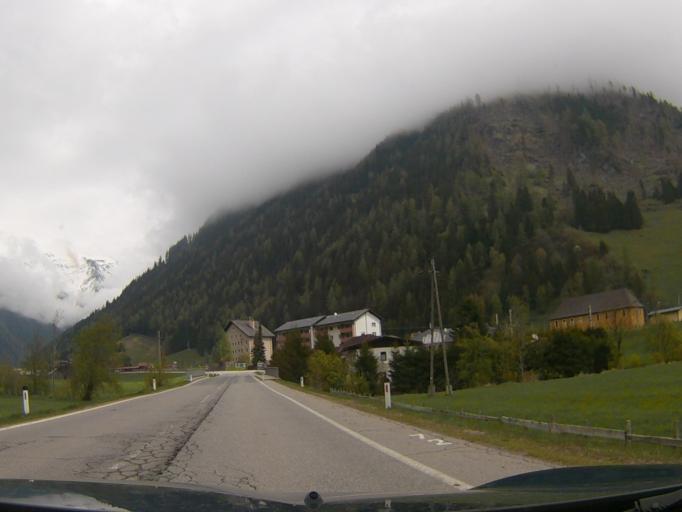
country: AT
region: Carinthia
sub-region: Politischer Bezirk Spittal an der Drau
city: Obervellach
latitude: 46.9760
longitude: 13.1765
